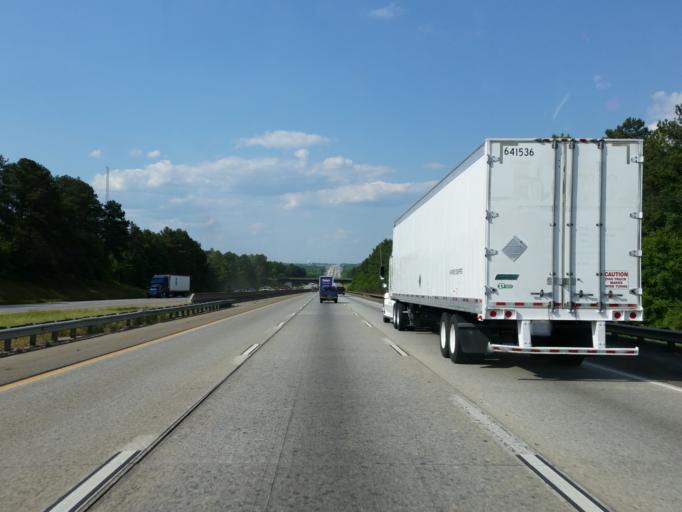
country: US
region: Georgia
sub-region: Peach County
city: Byron
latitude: 32.6807
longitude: -83.7422
